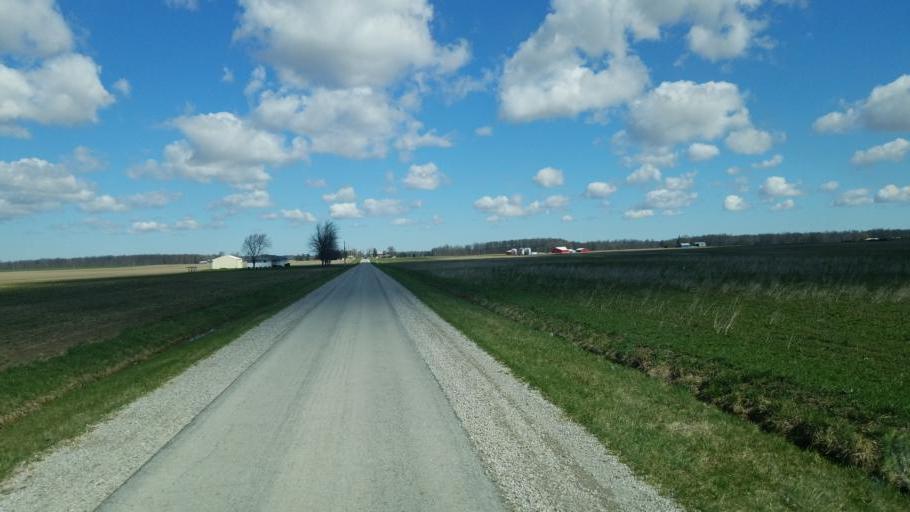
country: US
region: Ohio
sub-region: Sandusky County
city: Mount Carmel
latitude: 41.1007
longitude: -82.9383
